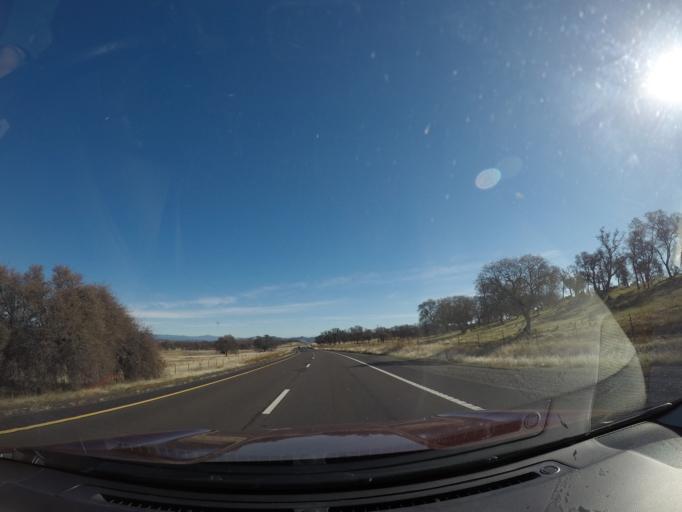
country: US
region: California
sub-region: Calaveras County
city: Copperopolis
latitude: 37.8472
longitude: -120.5756
